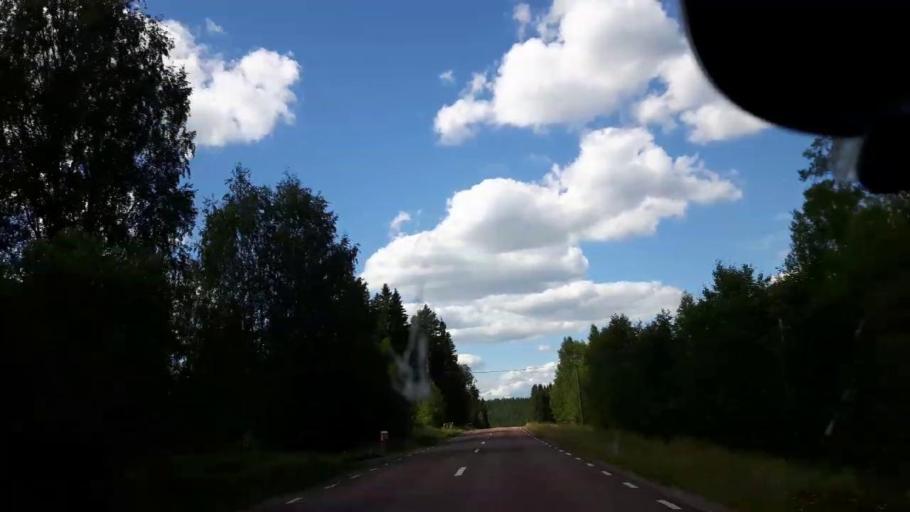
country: SE
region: Jaemtland
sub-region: Ragunda Kommun
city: Hammarstrand
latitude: 63.0195
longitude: 16.5568
